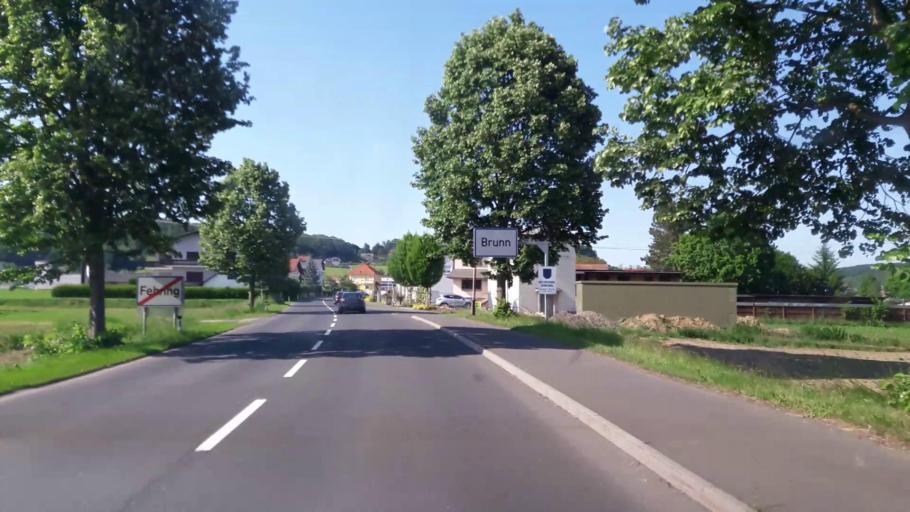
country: AT
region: Styria
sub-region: Politischer Bezirk Suedoststeiermark
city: Fehring
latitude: 46.9462
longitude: 16.0094
